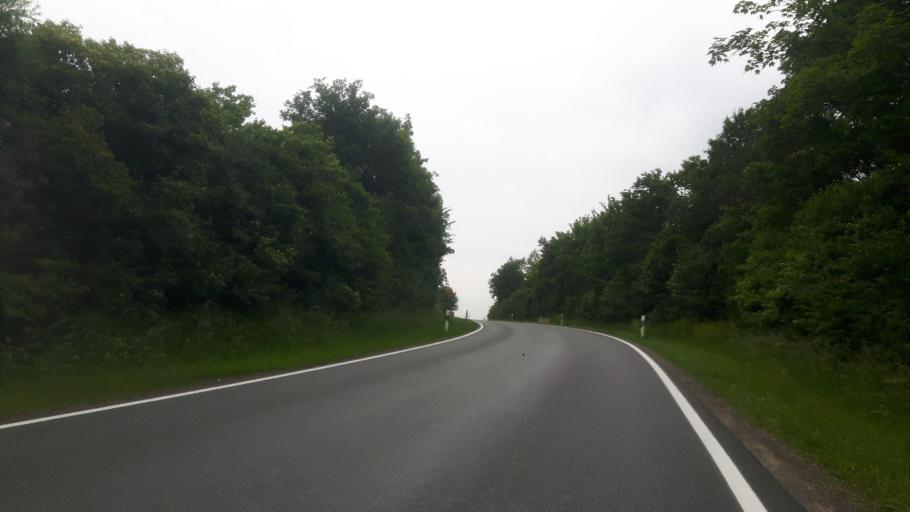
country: DE
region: Bavaria
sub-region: Regierungsbezirk Unterfranken
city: Schwanfeld
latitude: 49.8995
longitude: 10.1253
